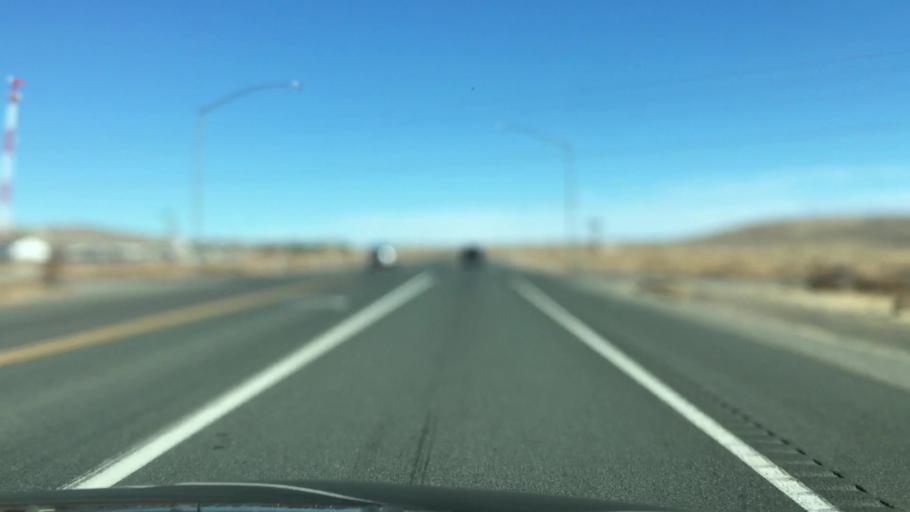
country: US
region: Nevada
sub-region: Lyon County
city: Stagecoach
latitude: 39.3610
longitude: -119.3754
